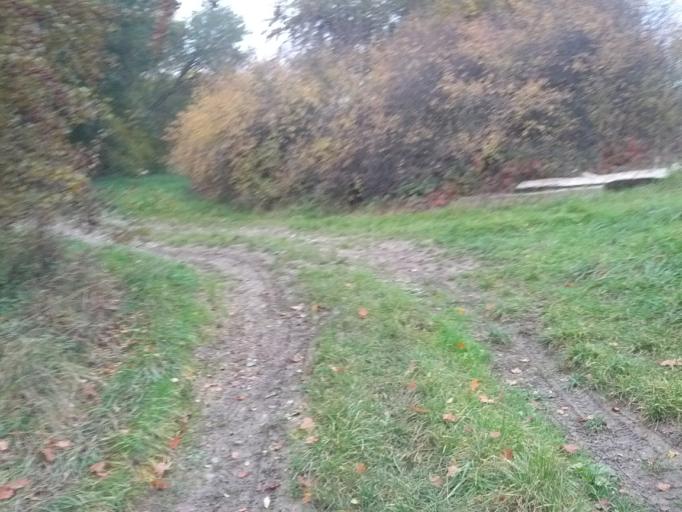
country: DE
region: Thuringia
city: Eisenach
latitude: 50.9941
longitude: 10.3639
